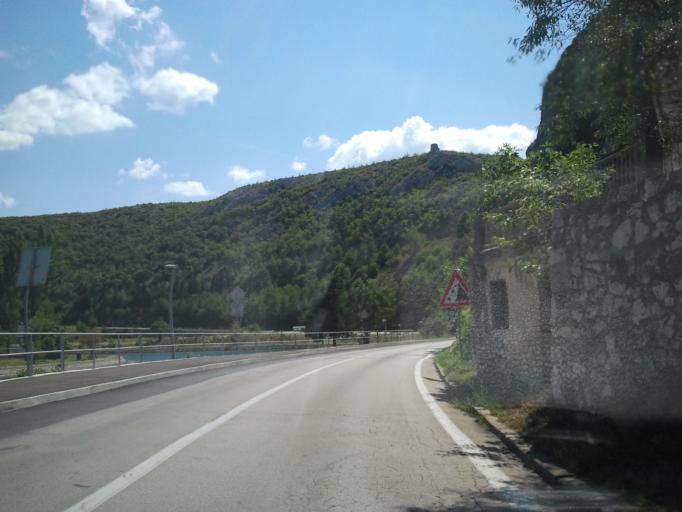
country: HR
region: Zadarska
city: Obrovac
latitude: 44.2008
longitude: 15.6838
